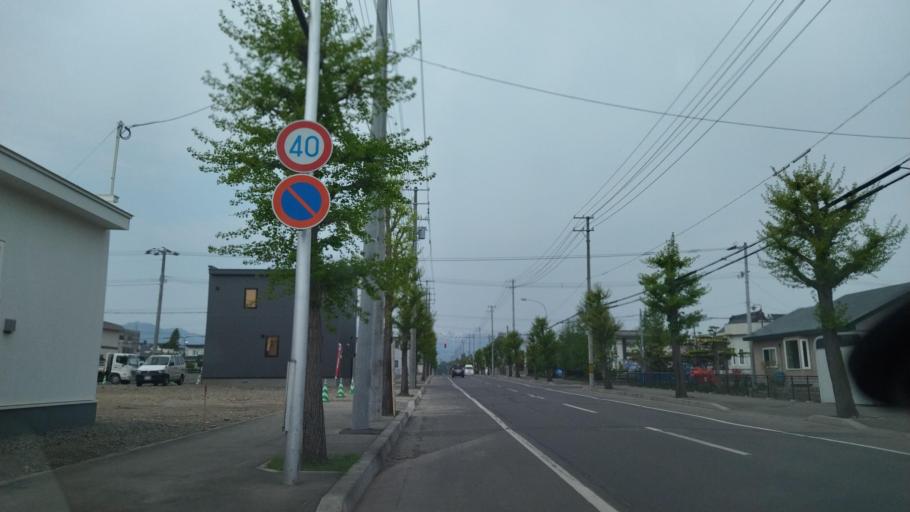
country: JP
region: Hokkaido
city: Obihiro
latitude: 42.9159
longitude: 143.0506
